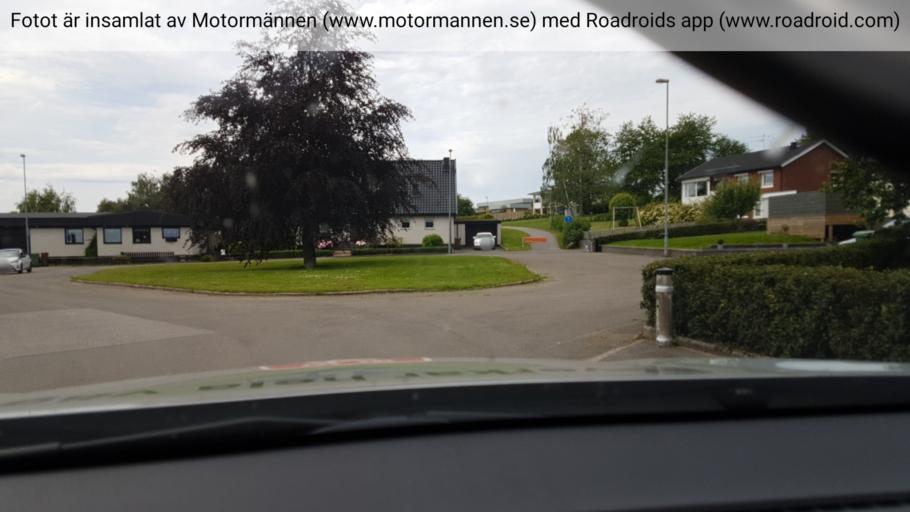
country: SE
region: Vaestra Goetaland
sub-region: Falkopings Kommun
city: Falkoeping
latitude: 58.1690
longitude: 13.5321
